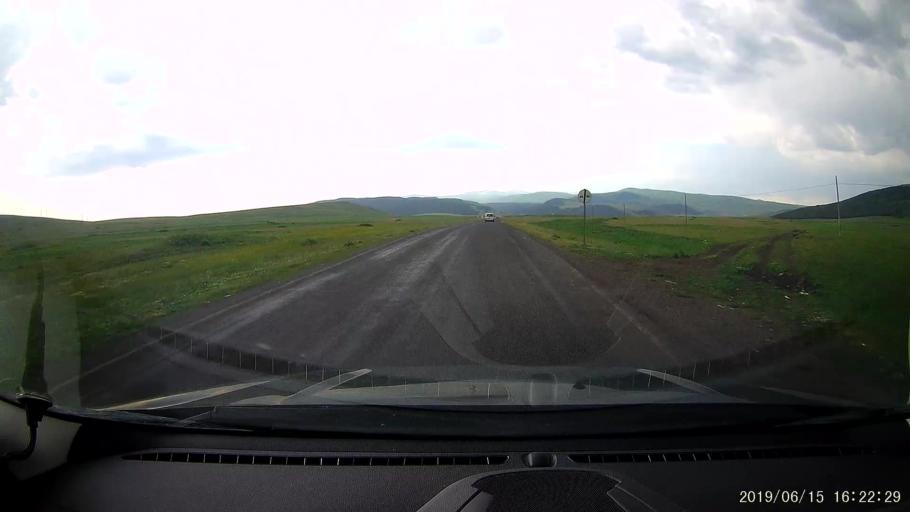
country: TR
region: Ardahan
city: Hanak
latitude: 41.1877
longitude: 42.8511
